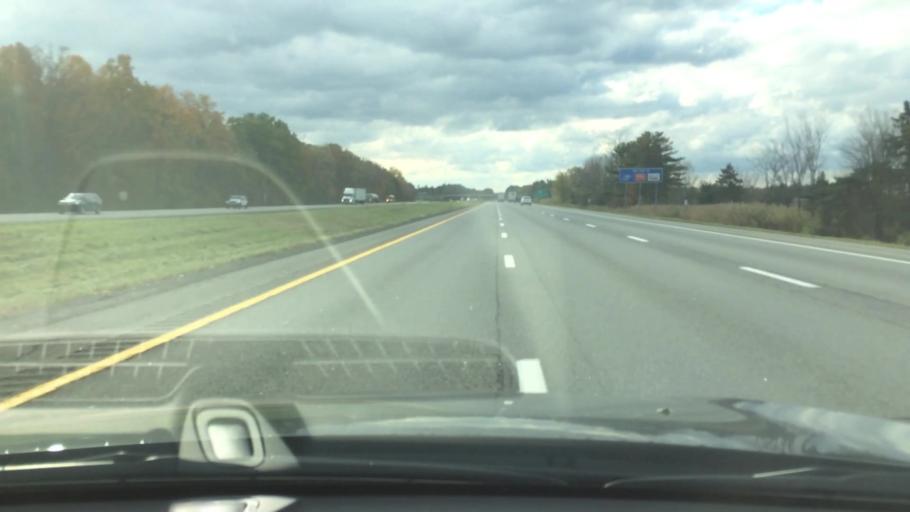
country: US
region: New York
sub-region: Saratoga County
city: Ballston Spa
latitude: 42.9788
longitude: -73.8029
